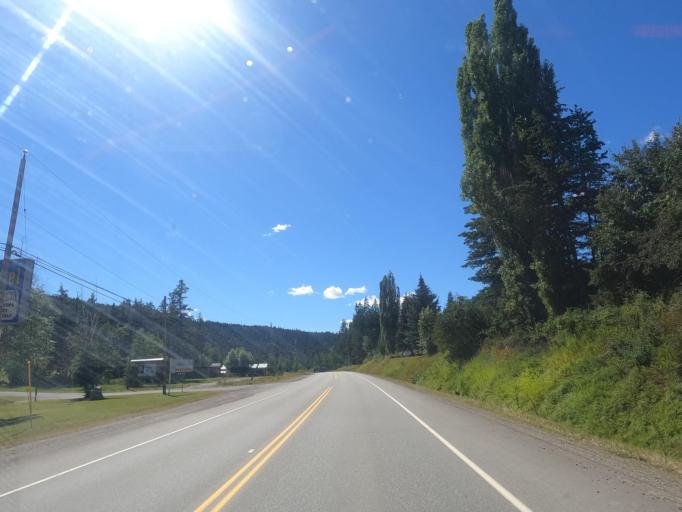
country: CA
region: British Columbia
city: Williams Lake
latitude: 52.4256
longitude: -122.3080
